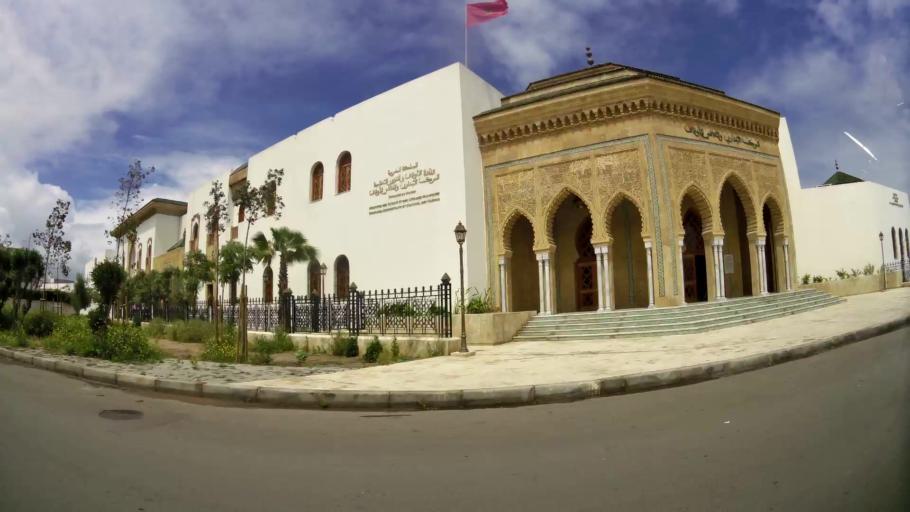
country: MA
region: Grand Casablanca
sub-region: Casablanca
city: Casablanca
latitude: 33.5661
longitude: -7.6352
